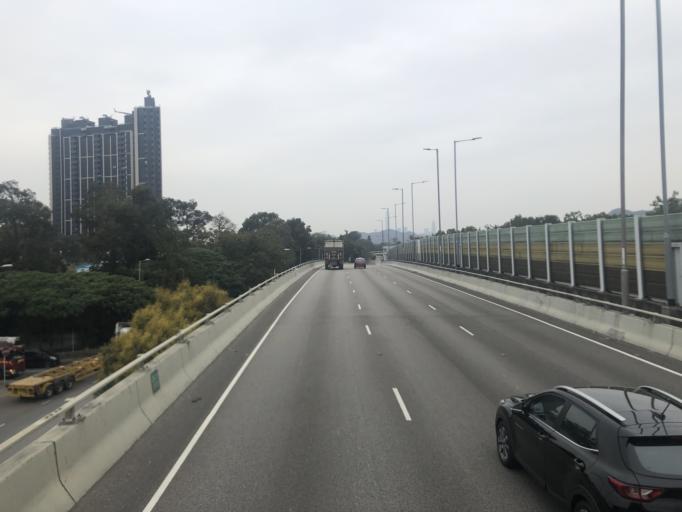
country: HK
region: Tai Po
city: Tai Po
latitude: 22.4999
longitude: 114.1241
